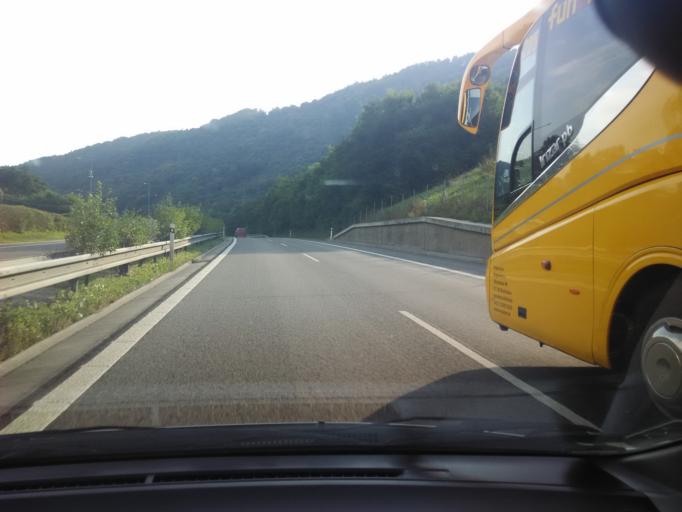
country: SK
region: Banskobystricky
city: Zarnovica
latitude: 48.4630
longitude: 18.6912
